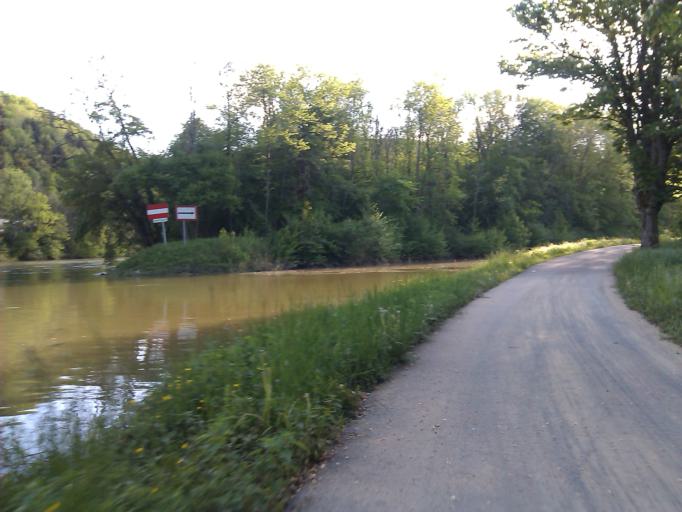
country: FR
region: Franche-Comte
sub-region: Departement du Doubs
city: Clerval
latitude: 47.3973
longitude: 6.5050
